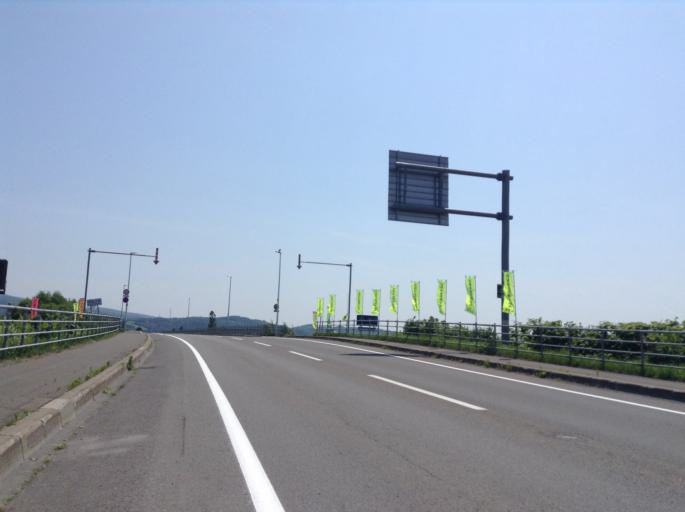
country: JP
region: Hokkaido
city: Nayoro
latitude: 44.3613
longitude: 142.4397
